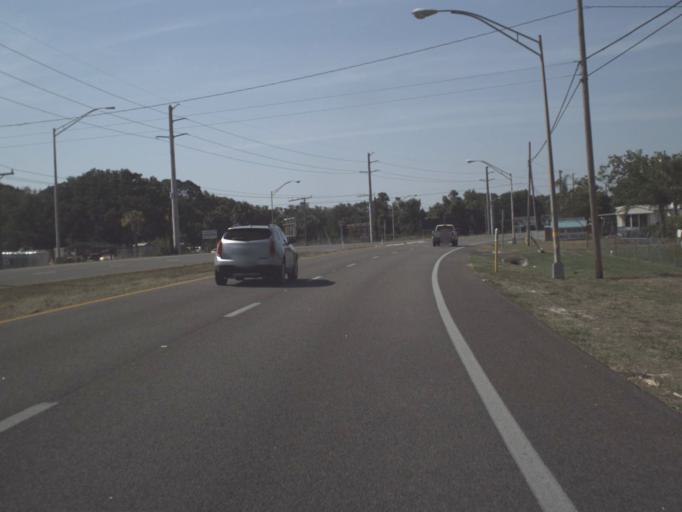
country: US
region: Florida
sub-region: Brevard County
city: Port Saint John
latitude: 28.5051
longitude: -80.7841
